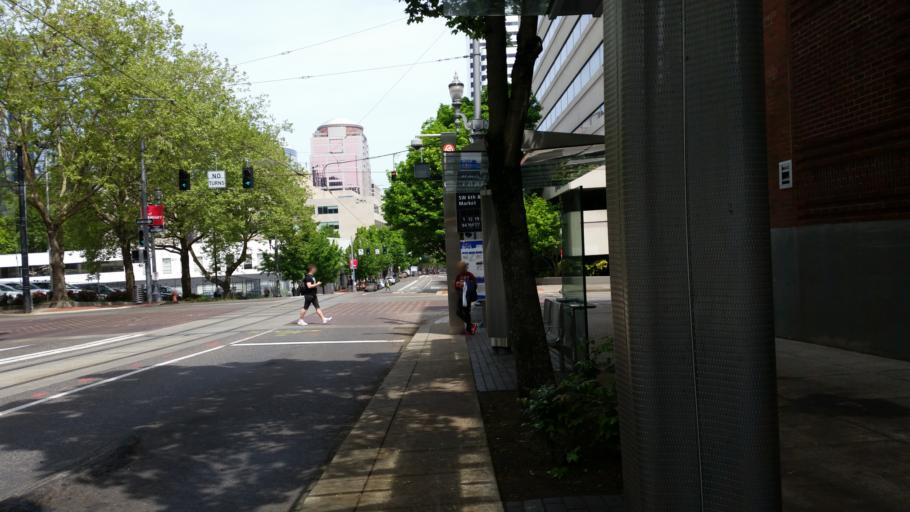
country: US
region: Oregon
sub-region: Multnomah County
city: Portland
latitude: 45.5129
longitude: -122.6821
